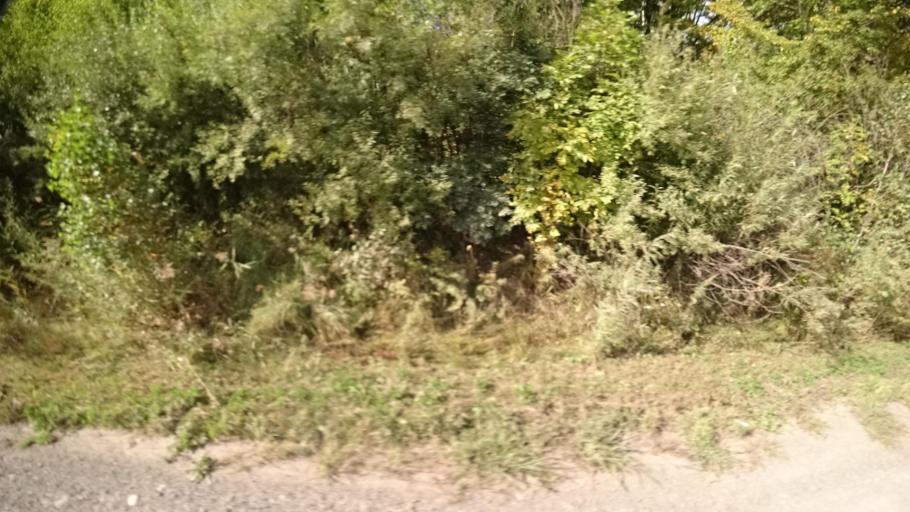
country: RU
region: Primorskiy
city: Yakovlevka
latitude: 44.3897
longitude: 133.5466
